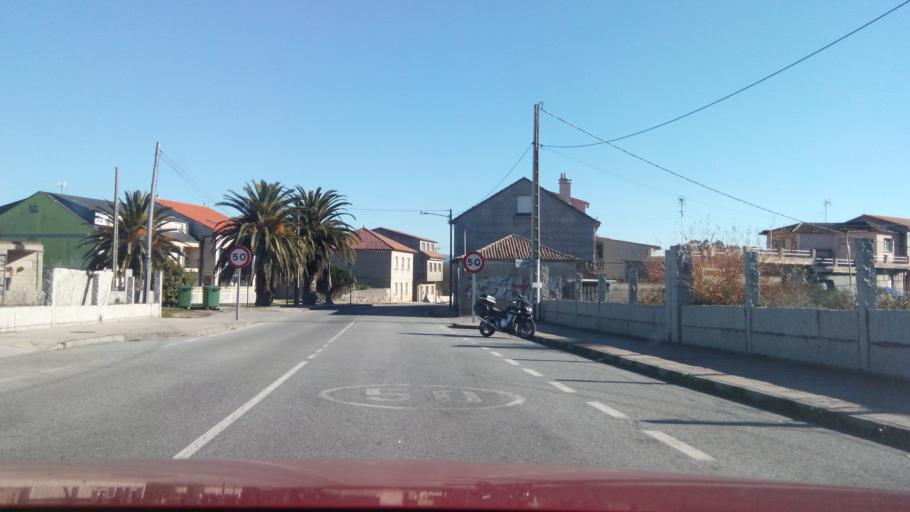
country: ES
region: Galicia
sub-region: Provincia de Pontevedra
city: O Grove
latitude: 42.4683
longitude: -8.9212
